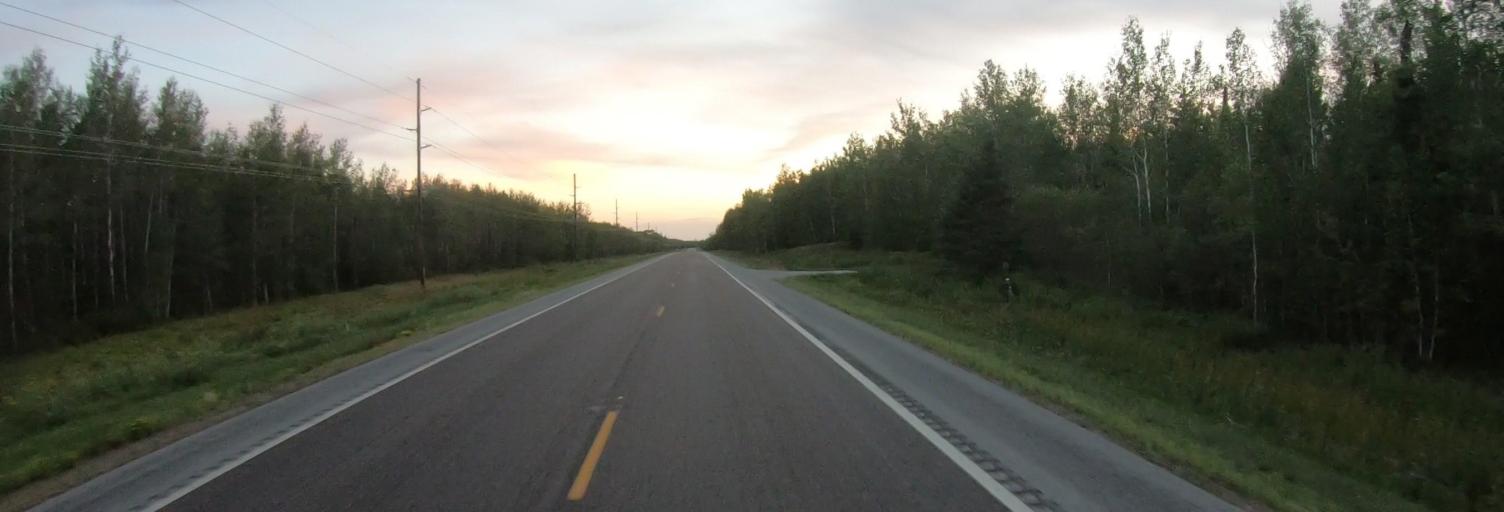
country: US
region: Minnesota
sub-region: Saint Louis County
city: Virginia
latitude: 47.8522
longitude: -92.4956
